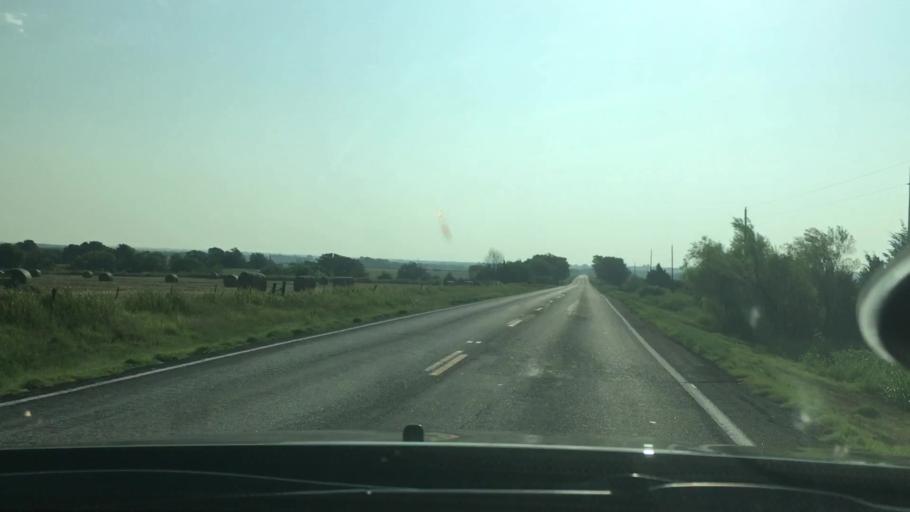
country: US
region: Oklahoma
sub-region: Bryan County
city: Durant
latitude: 34.1427
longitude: -96.3060
